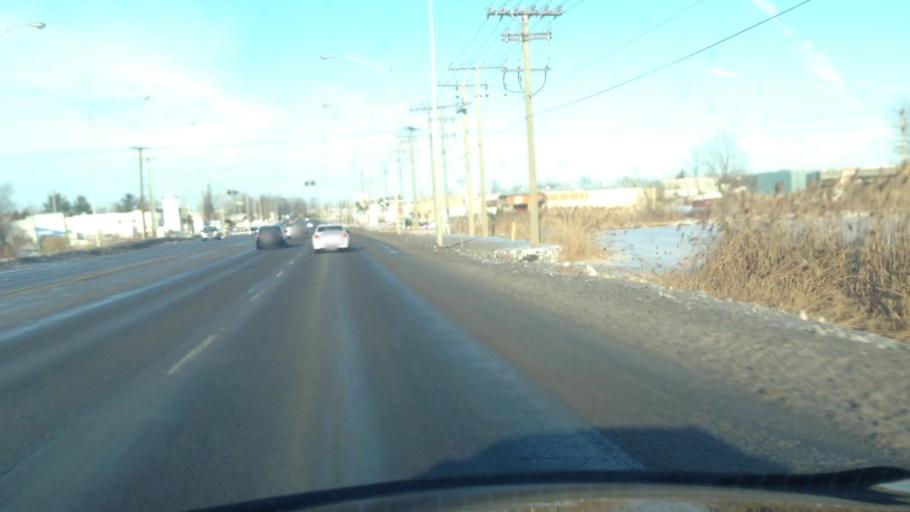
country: CA
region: Quebec
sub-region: Laurentides
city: Saint-Jerome
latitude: 45.7535
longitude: -73.9975
